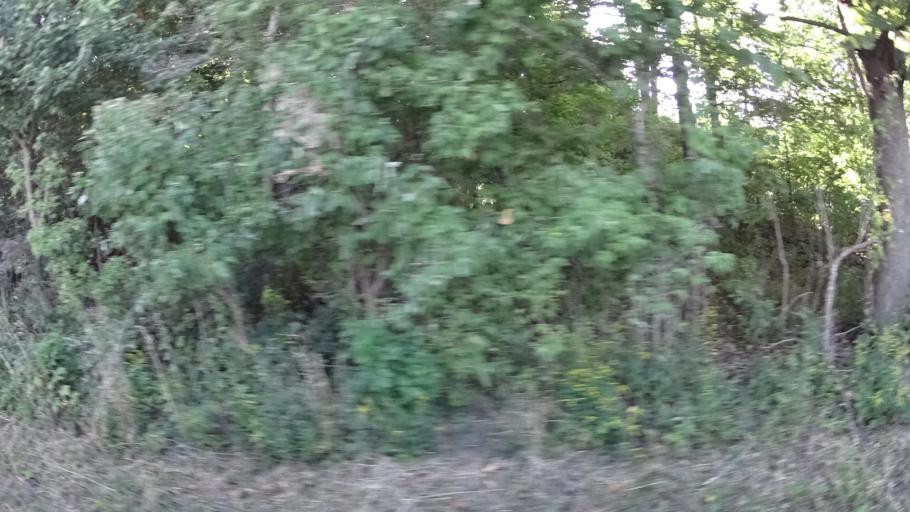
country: US
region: Ohio
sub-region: Erie County
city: Sandusky
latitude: 41.6123
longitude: -82.7226
